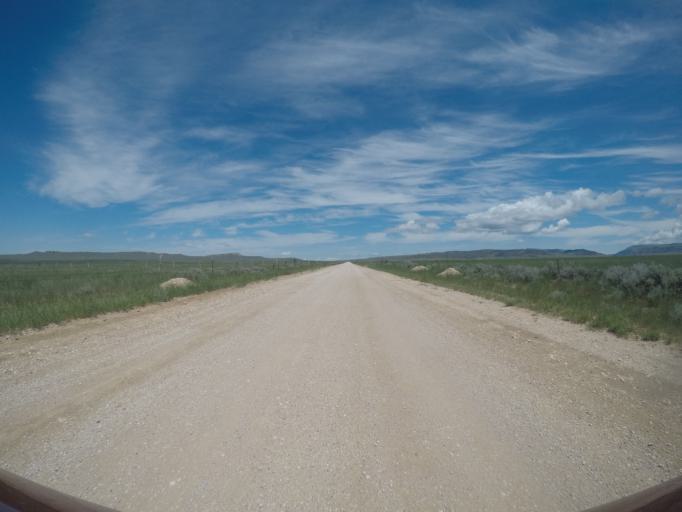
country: US
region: Wyoming
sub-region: Park County
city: Powell
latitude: 45.2118
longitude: -108.7191
